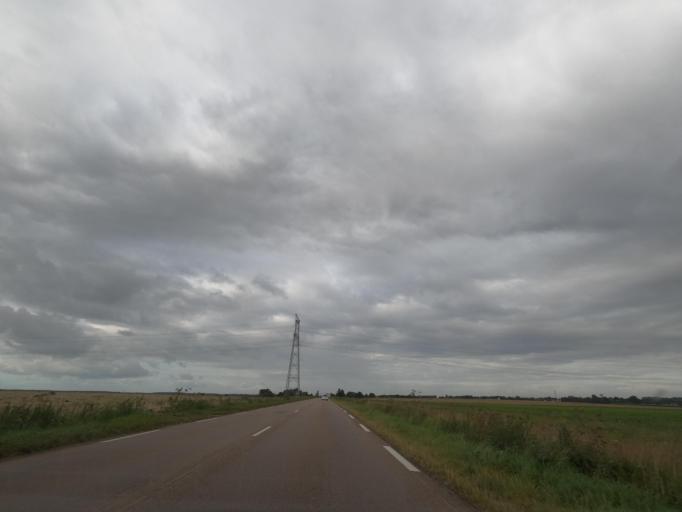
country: FR
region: Haute-Normandie
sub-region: Departement de l'Eure
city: Bourgtheroulde-Infreville
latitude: 49.2905
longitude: 0.8574
